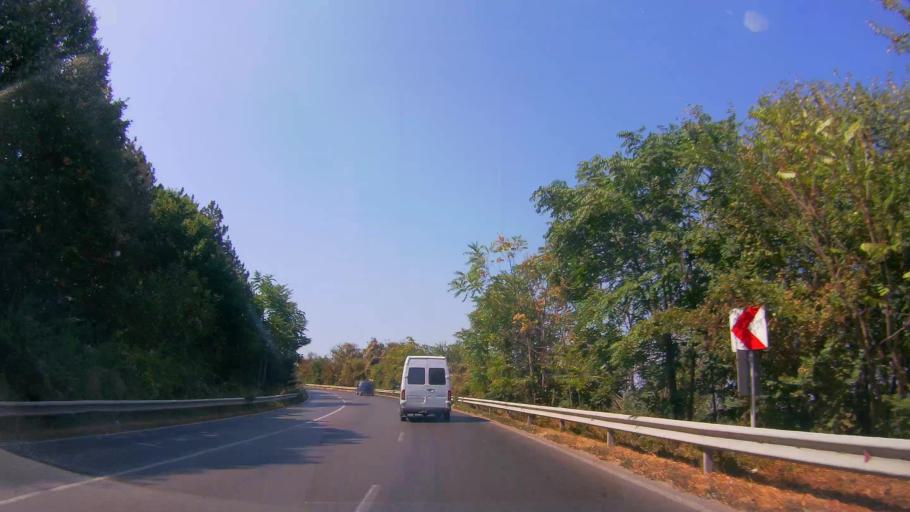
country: BG
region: Razgrad
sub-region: Obshtina Tsar Kaloyan
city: Tsar Kaloyan
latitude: 43.6273
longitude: 26.2117
